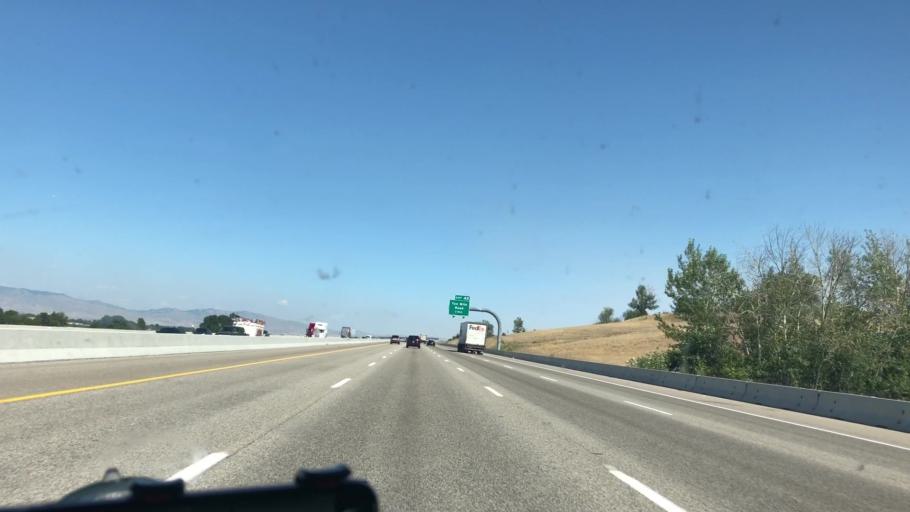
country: US
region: Idaho
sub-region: Ada County
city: Meridian
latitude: 43.5959
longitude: -116.4643
